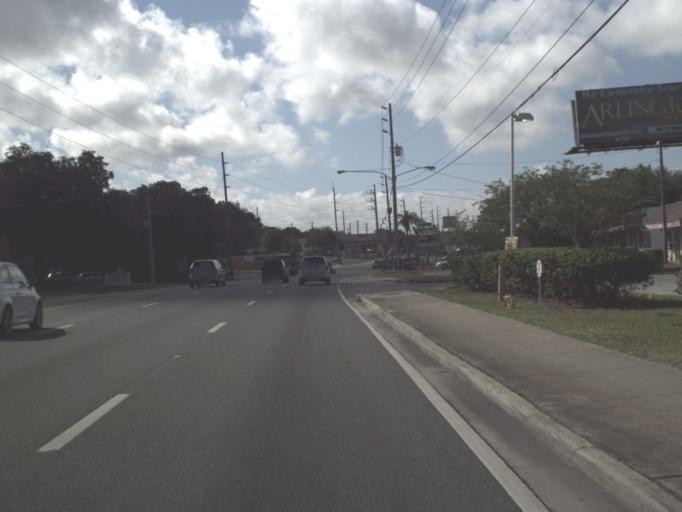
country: US
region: Florida
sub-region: Lake County
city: Fruitland Park
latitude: 28.8414
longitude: -81.8949
